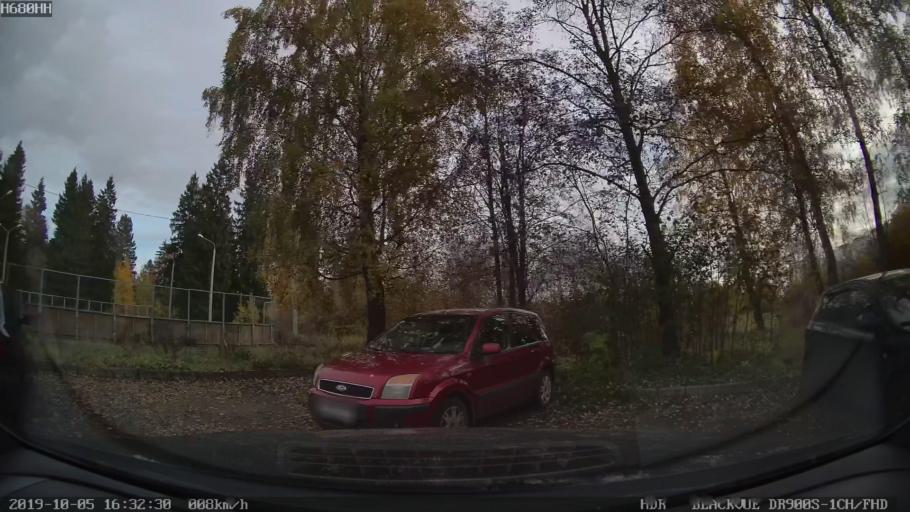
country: RU
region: Moskovskaya
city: Solnechnogorsk
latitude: 56.2166
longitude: 37.0328
